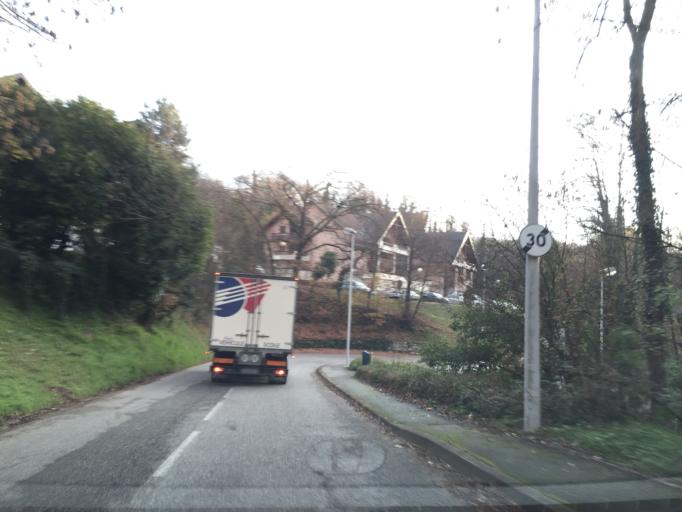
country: FR
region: Rhone-Alpes
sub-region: Departement de la Savoie
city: Sonnaz
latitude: 45.5986
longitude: 5.9087
